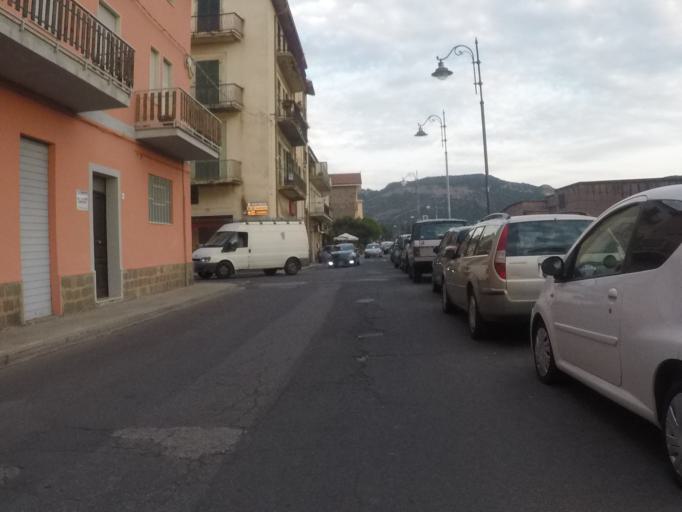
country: IT
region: Sardinia
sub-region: Provincia di Oristano
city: Bosa
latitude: 40.2958
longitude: 8.4987
